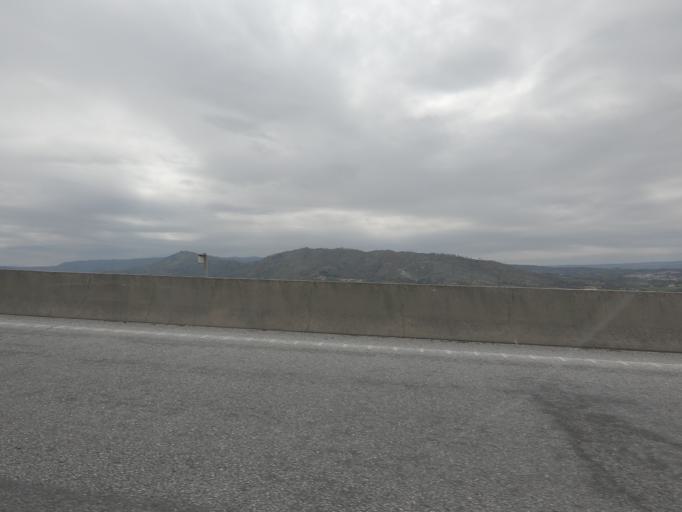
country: PT
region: Guarda
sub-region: Guarda
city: Guarda
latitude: 40.6119
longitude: -7.2838
